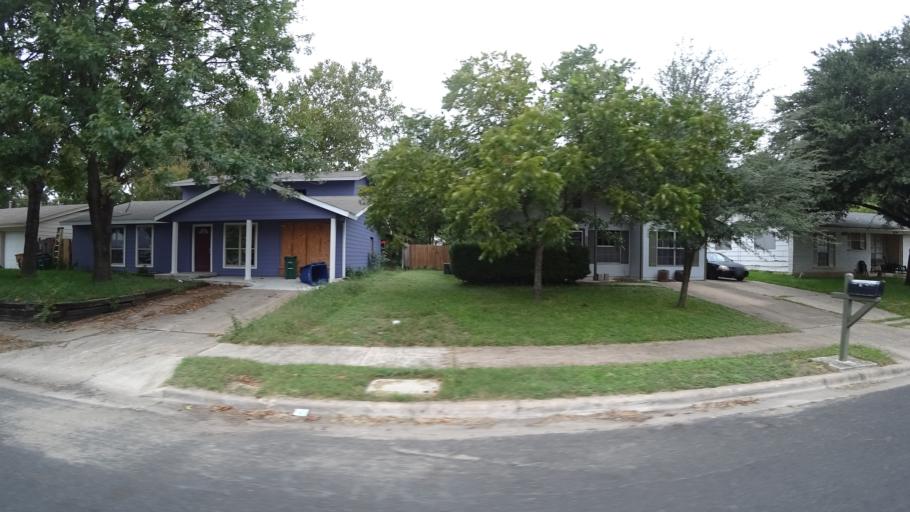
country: US
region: Texas
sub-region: Travis County
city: Onion Creek
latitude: 30.2006
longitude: -97.7779
